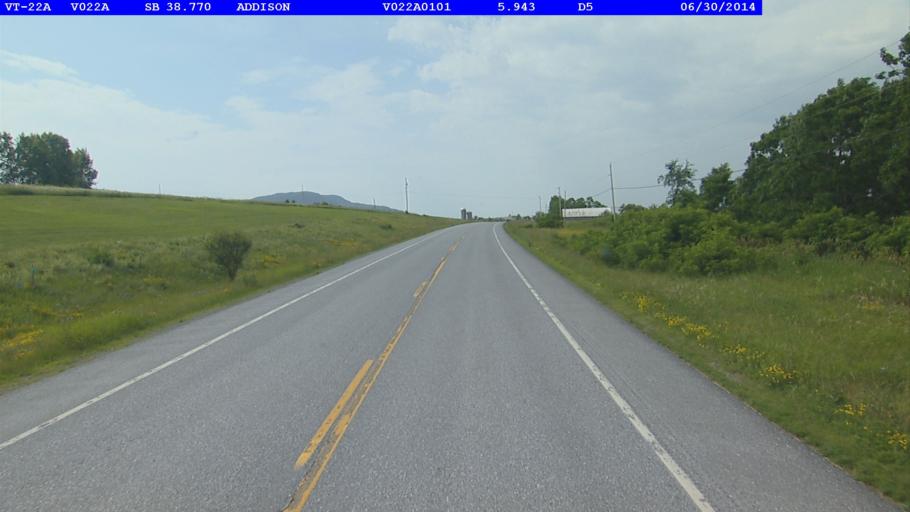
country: US
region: Vermont
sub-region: Addison County
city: Vergennes
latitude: 44.1143
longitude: -73.2937
